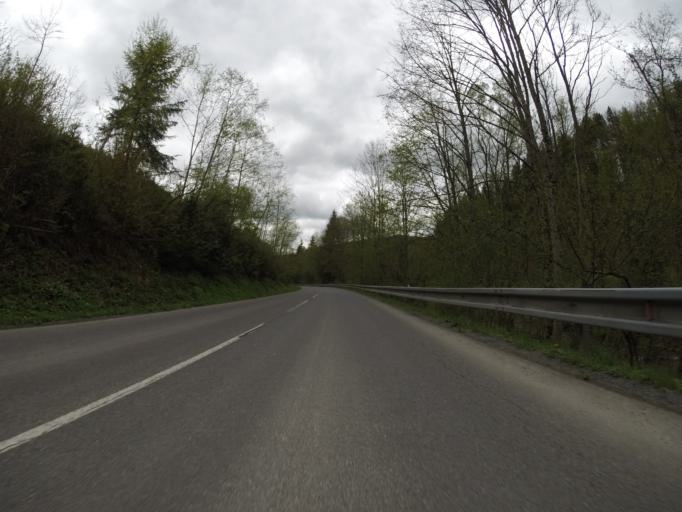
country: SK
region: Banskobystricky
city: Hrinova
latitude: 48.6078
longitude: 19.5691
